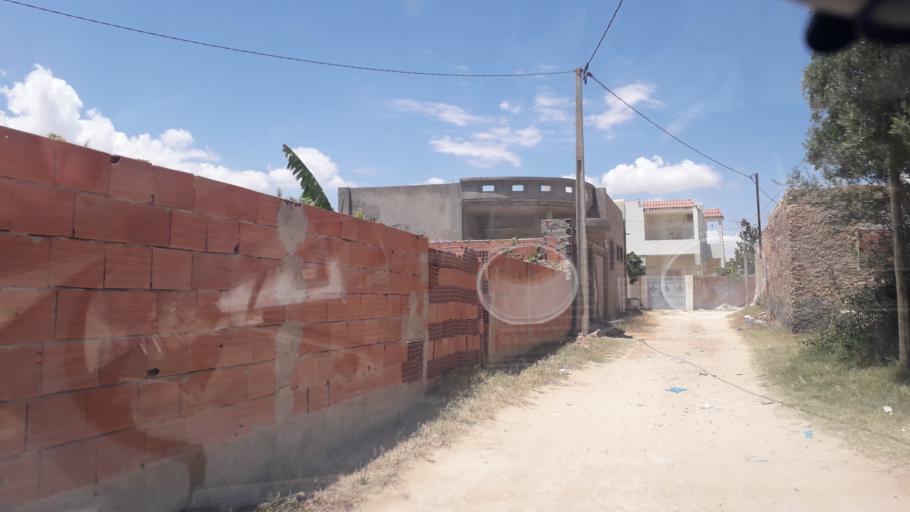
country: TN
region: Safaqis
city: Al Qarmadah
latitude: 34.8180
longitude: 10.7677
